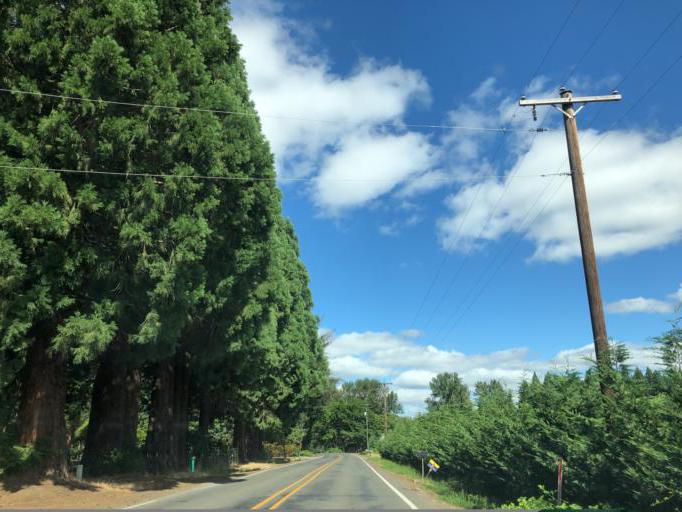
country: US
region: Oregon
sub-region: Marion County
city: Mount Angel
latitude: 45.1007
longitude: -122.7436
